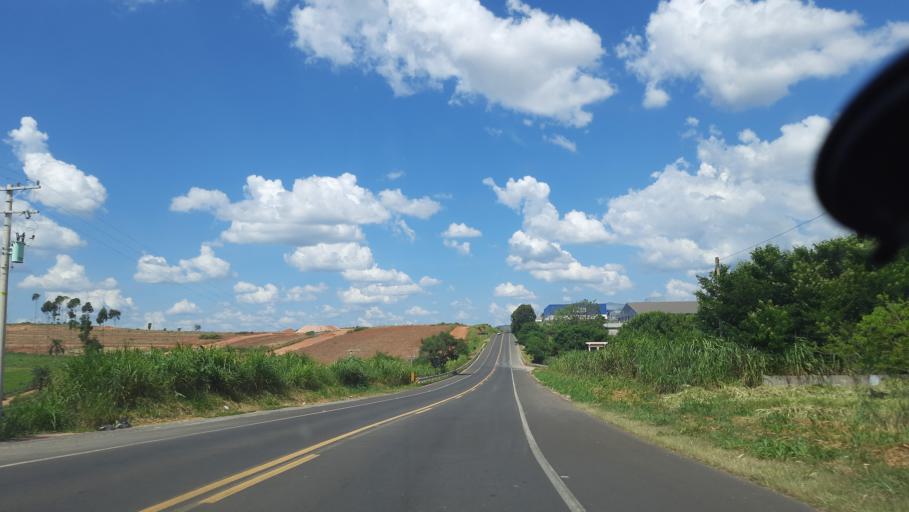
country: BR
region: Sao Paulo
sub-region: Sao Jose Do Rio Pardo
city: Sao Jose do Rio Pardo
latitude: -21.6033
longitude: -46.9250
